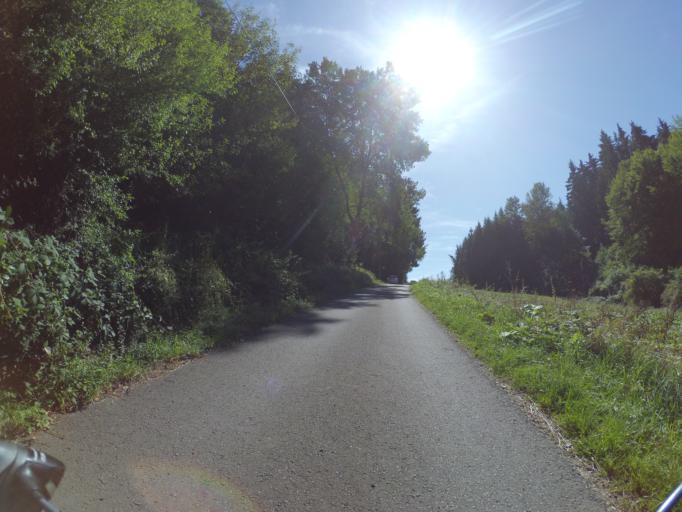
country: DE
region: Rheinland-Pfalz
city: Rorodt
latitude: 49.8098
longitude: 7.0680
